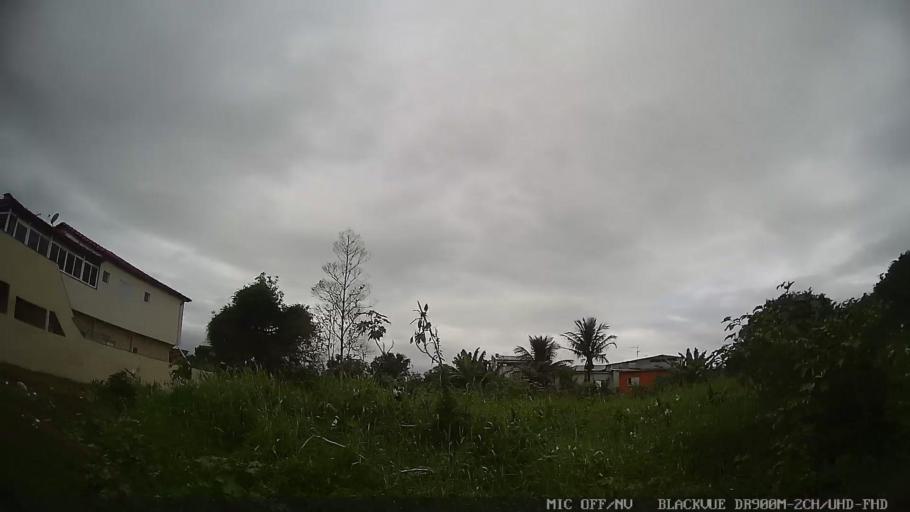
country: BR
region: Sao Paulo
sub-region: Itanhaem
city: Itanhaem
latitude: -24.2395
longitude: -46.8914
